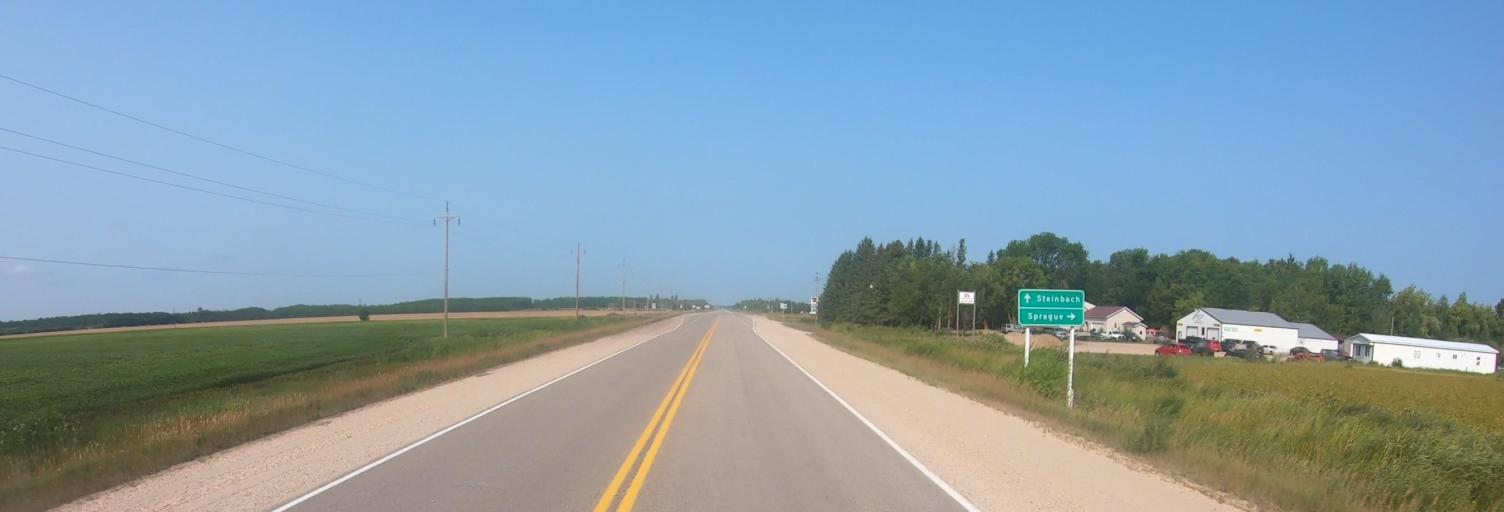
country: US
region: Minnesota
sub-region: Roseau County
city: Roseau
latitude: 49.0235
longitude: -95.6388
